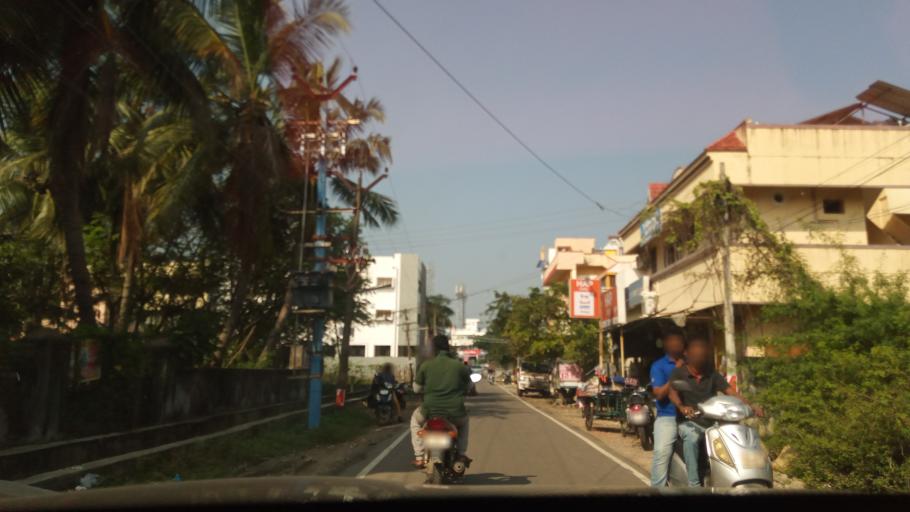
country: IN
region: Tamil Nadu
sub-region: Kancheepuram
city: Guduvancheri
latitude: 12.8520
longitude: 80.0681
